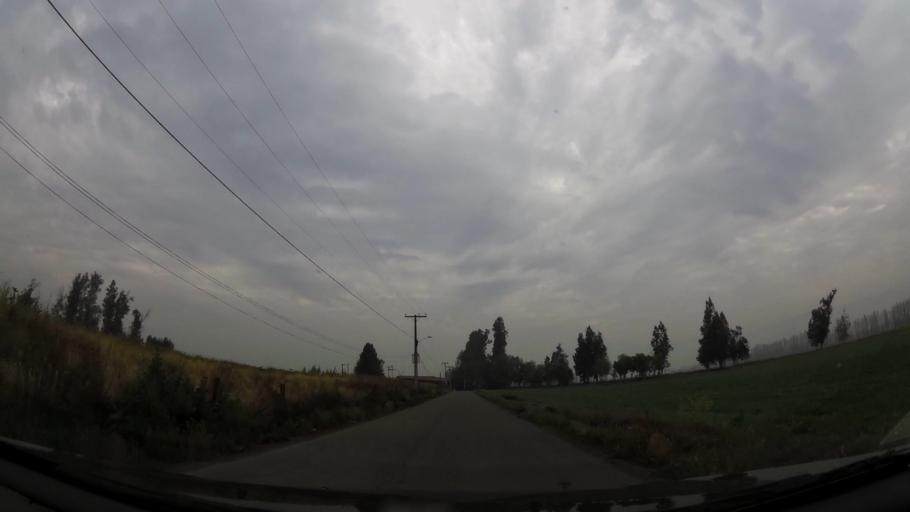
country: CL
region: Santiago Metropolitan
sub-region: Provincia de Chacabuco
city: Lampa
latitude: -33.2627
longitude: -70.7676
